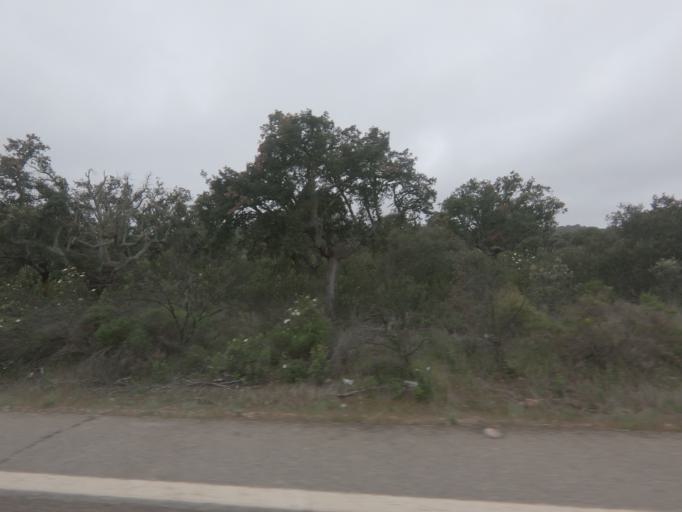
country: ES
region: Extremadura
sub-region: Provincia de Badajoz
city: Puebla de Obando
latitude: 39.2807
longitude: -6.5213
